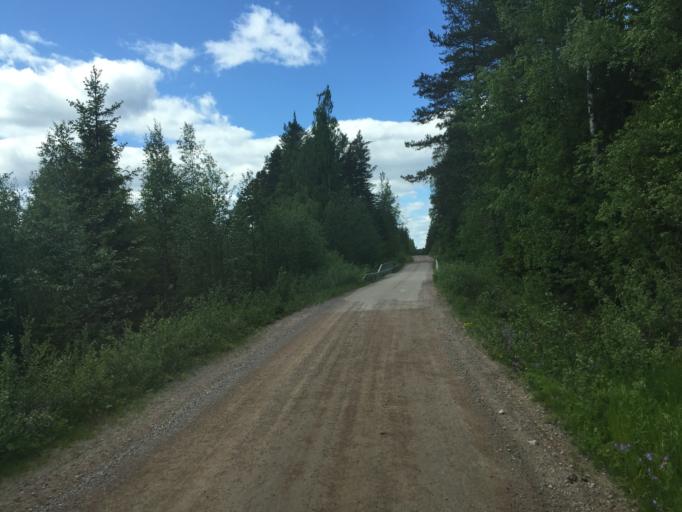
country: SE
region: Dalarna
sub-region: Vansbro Kommun
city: Vansbro
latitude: 60.4434
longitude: 14.1794
